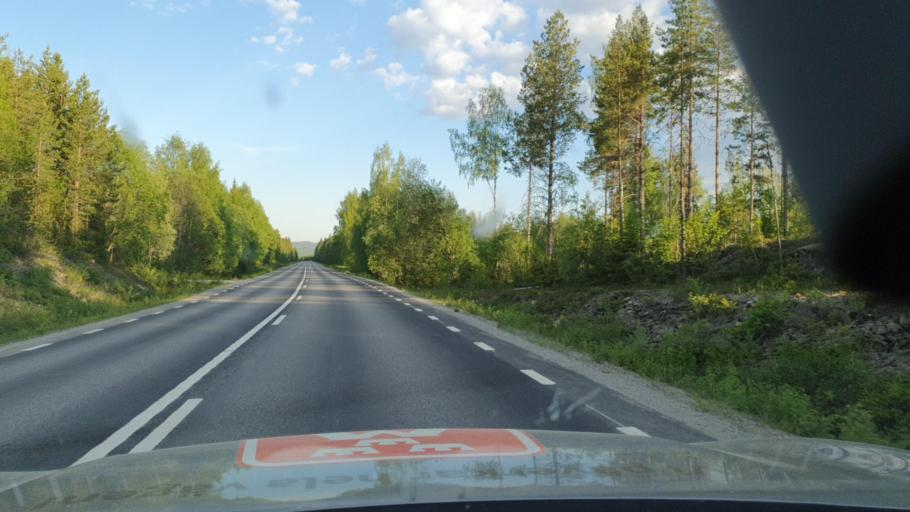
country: SE
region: Vaesternorrland
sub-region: Solleftea Kommun
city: As
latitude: 63.6549
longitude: 16.7875
